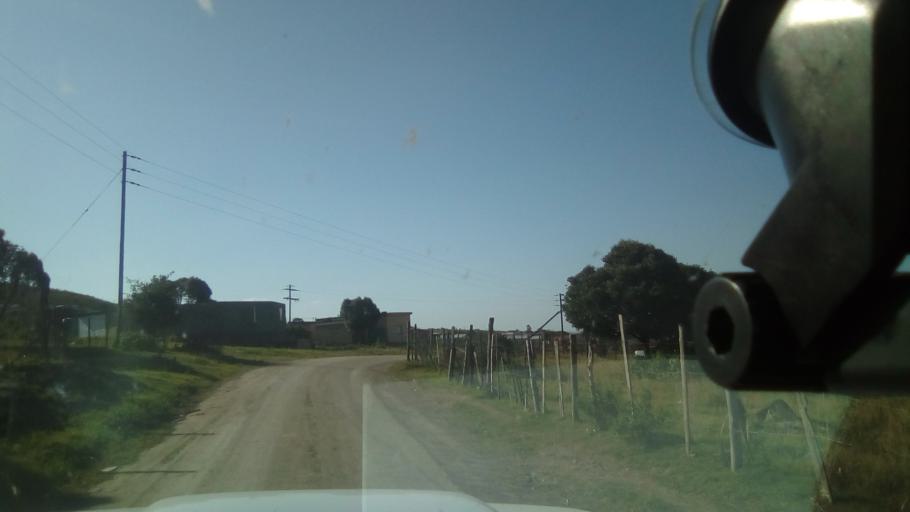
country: ZA
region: Eastern Cape
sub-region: Buffalo City Metropolitan Municipality
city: Bhisho
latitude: -32.8143
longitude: 27.3531
